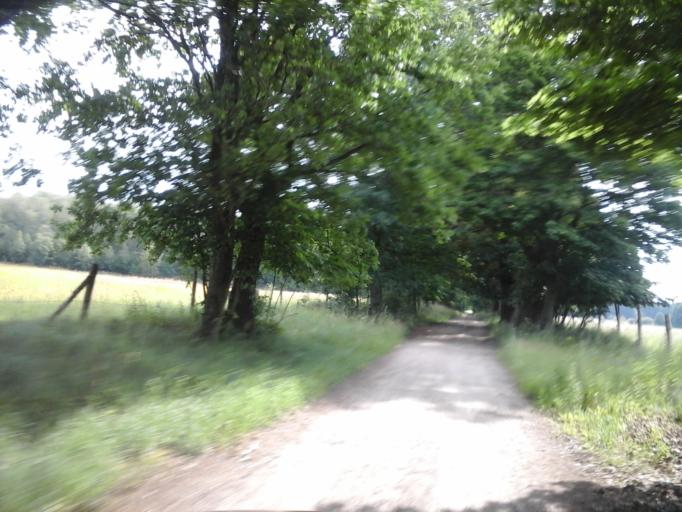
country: PL
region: West Pomeranian Voivodeship
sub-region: Powiat choszczenski
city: Recz
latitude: 53.2422
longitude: 15.6277
